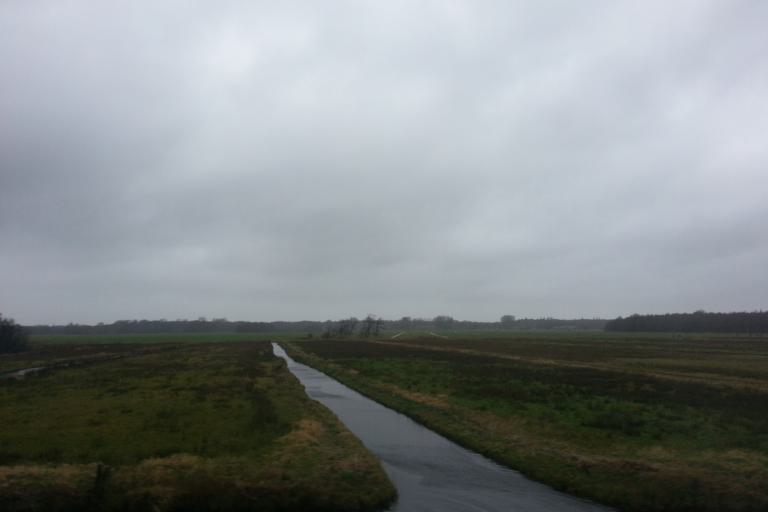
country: NL
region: South Holland
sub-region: Gemeente Leidschendam-Voorburg
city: Voorburg
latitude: 52.0979
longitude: 4.3854
